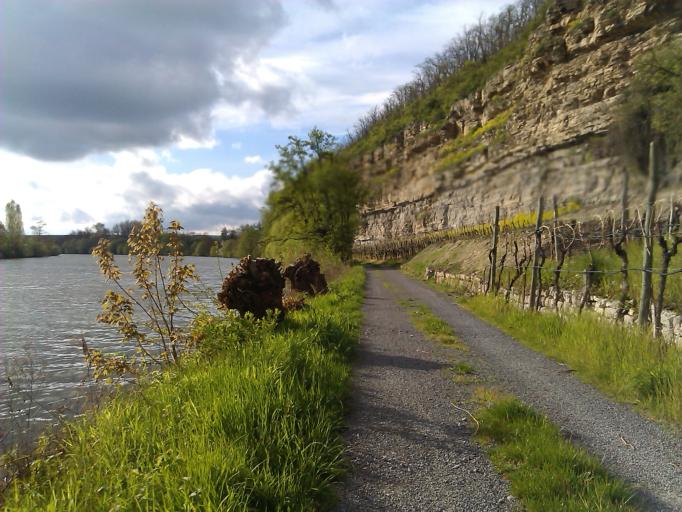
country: DE
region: Baden-Wuerttemberg
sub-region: Regierungsbezirk Stuttgart
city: Talheim
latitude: 49.0894
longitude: 9.1765
